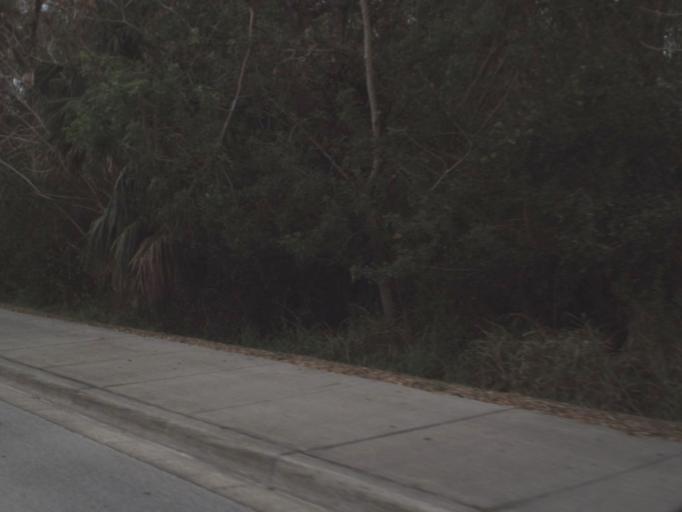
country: US
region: Florida
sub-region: Saint Lucie County
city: White City
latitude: 27.3782
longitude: -80.3503
